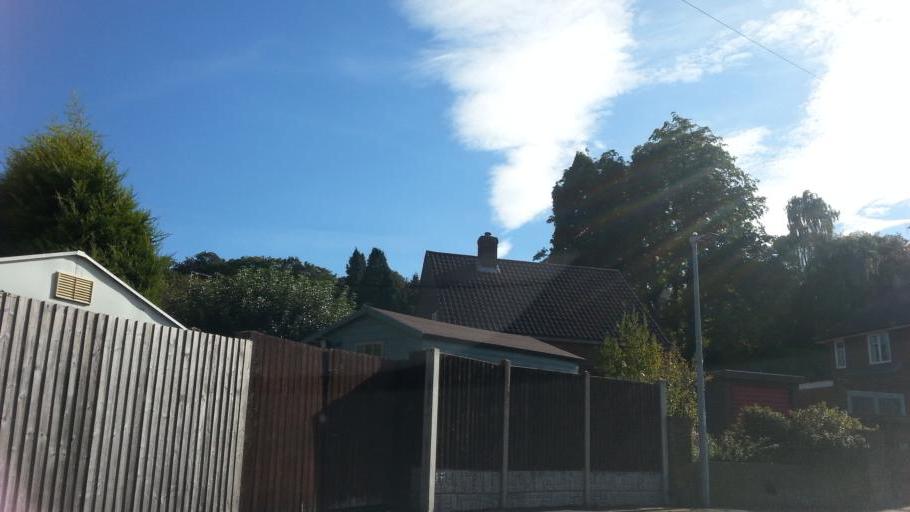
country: GB
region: England
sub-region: Telford and Wrekin
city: Wellington
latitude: 52.6925
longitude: -2.5234
